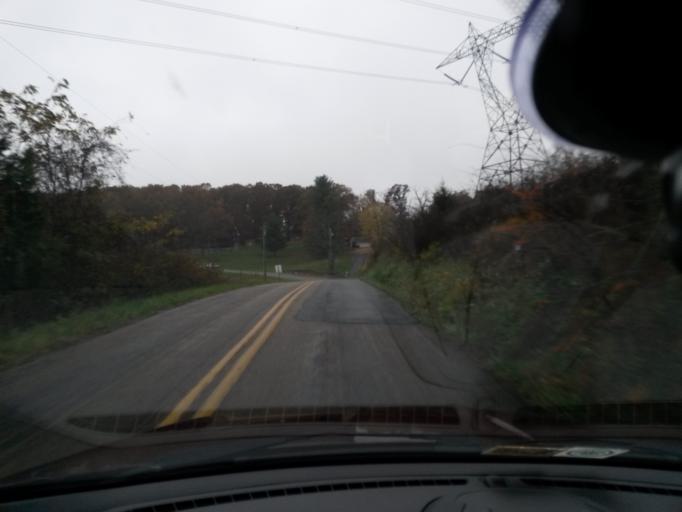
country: US
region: Virginia
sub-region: Botetourt County
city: Fincastle
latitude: 37.4726
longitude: -79.8447
